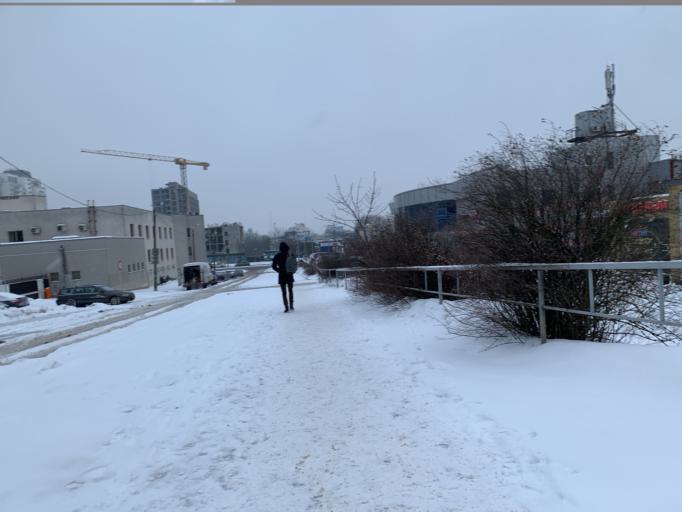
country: BY
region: Minsk
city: Minsk
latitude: 53.9293
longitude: 27.5888
